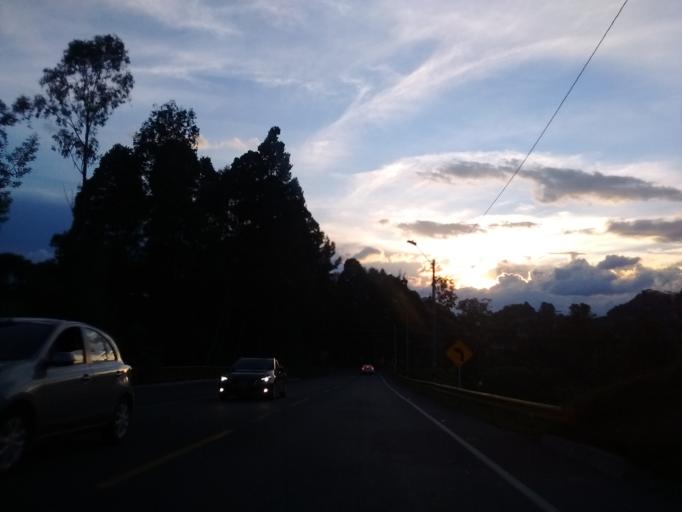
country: CO
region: Antioquia
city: Envigado
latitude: 6.1593
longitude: -75.5306
